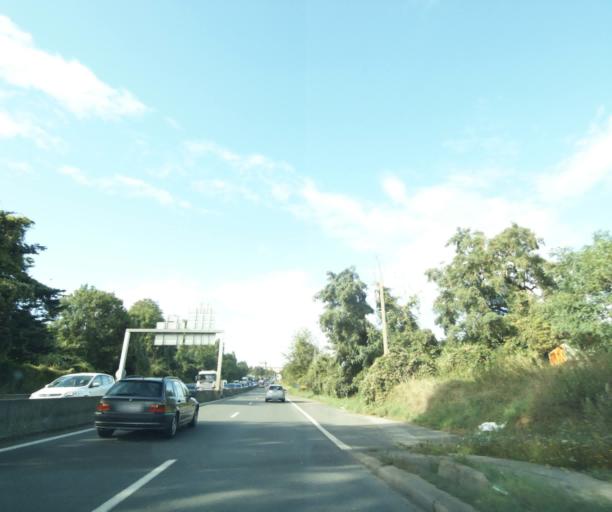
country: FR
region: Ile-de-France
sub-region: Departement de l'Essonne
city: Bievres
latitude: 48.7719
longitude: 2.2293
